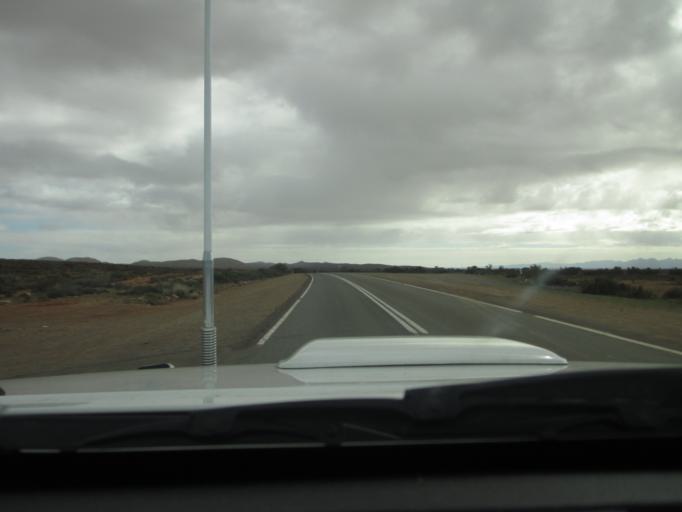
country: AU
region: South Australia
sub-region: Flinders Ranges
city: Quorn
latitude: -31.5560
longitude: 138.4281
